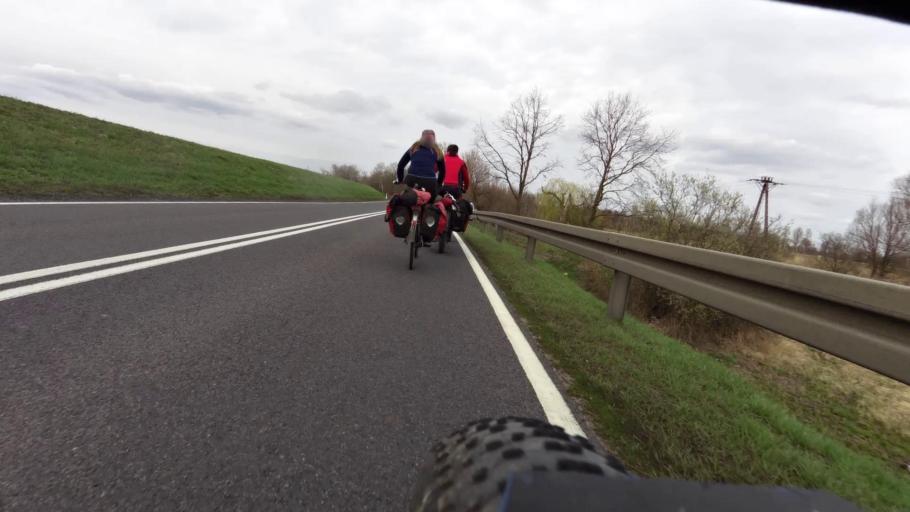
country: PL
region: Lubusz
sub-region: Powiat gorzowski
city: Kostrzyn nad Odra
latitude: 52.5681
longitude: 14.6421
